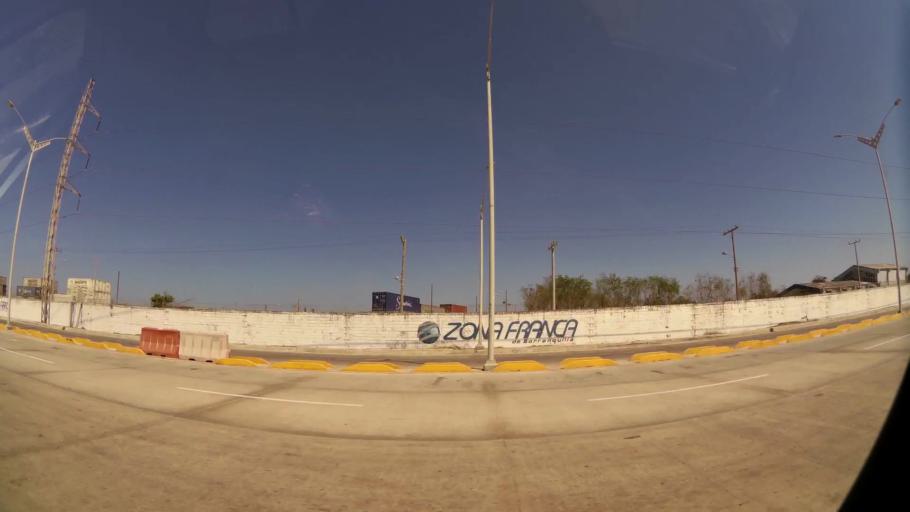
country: CO
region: Atlantico
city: Barranquilla
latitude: 10.9560
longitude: -74.7662
